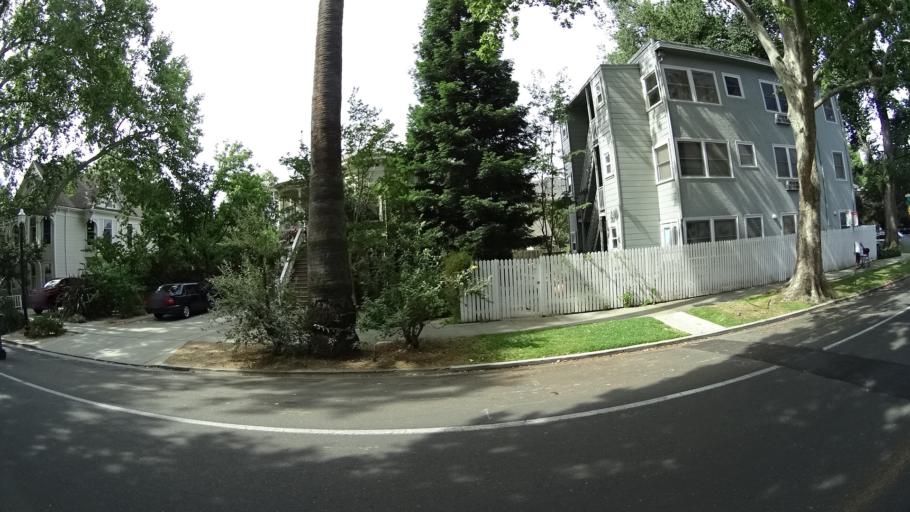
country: US
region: California
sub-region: Sacramento County
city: Sacramento
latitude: 38.5755
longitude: -121.4710
